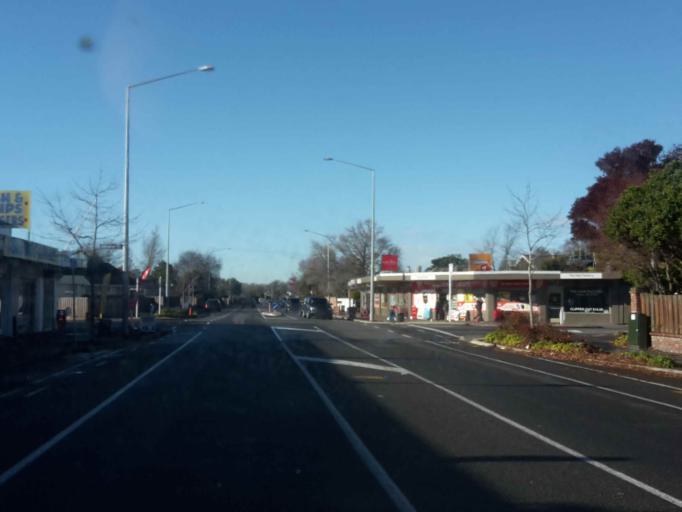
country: NZ
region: Canterbury
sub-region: Christchurch City
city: Christchurch
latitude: -43.5033
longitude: 172.5934
